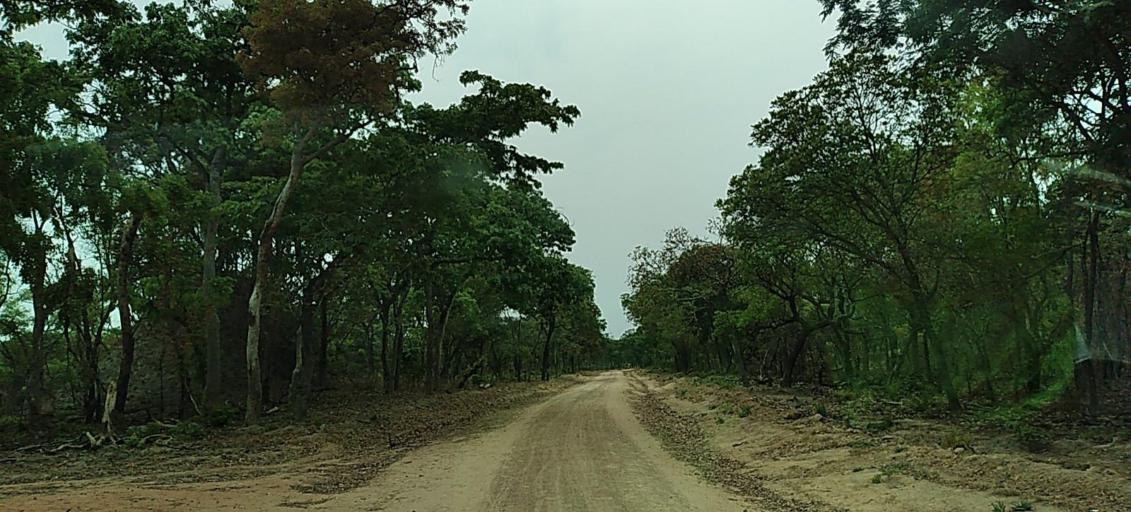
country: ZM
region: North-Western
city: Solwezi
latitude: -12.5415
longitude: 26.5263
